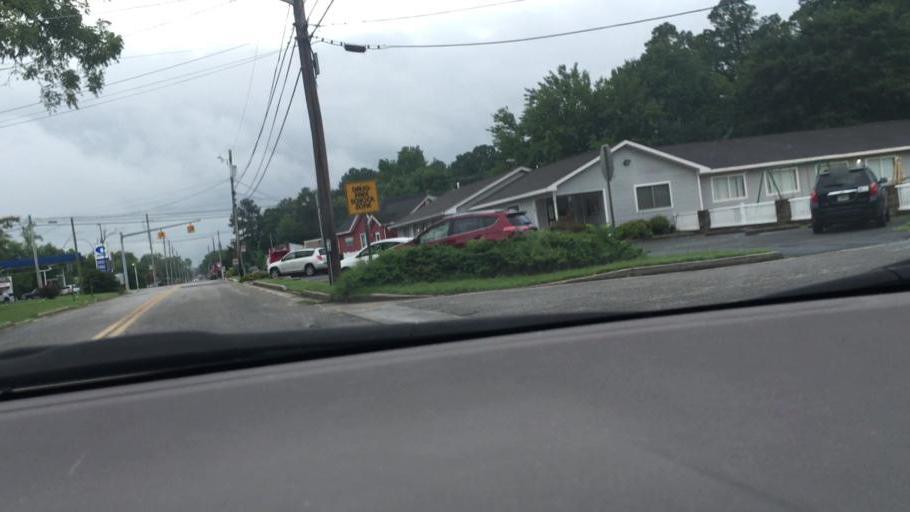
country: US
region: Maryland
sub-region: Wicomico County
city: Fruitland
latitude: 38.3286
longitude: -75.6242
